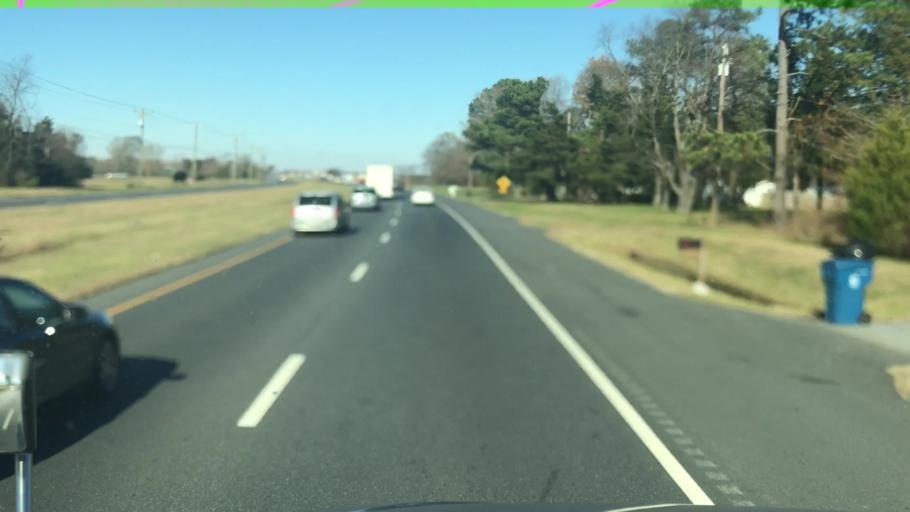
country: US
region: Delaware
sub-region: Sussex County
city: Bridgeville
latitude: 38.7055
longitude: -75.5882
